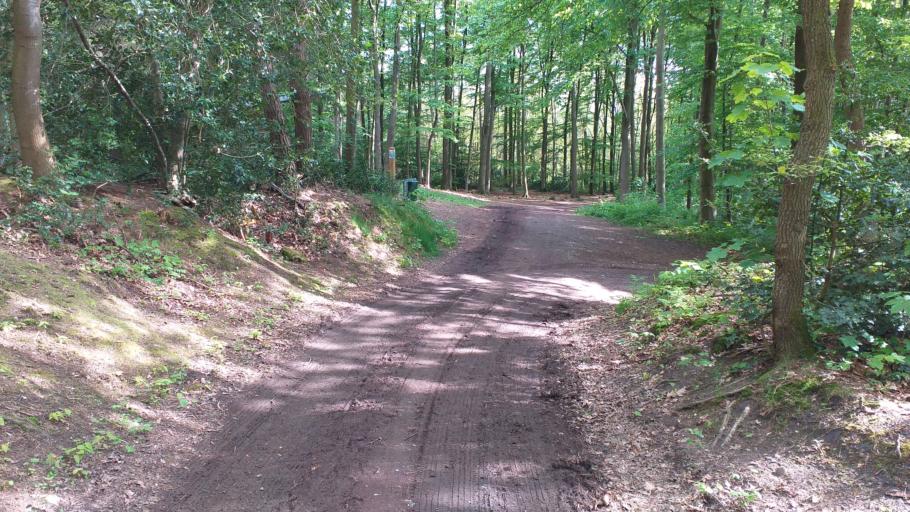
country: BE
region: Wallonia
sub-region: Province de Liege
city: La Calamine
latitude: 50.7195
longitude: 6.0529
